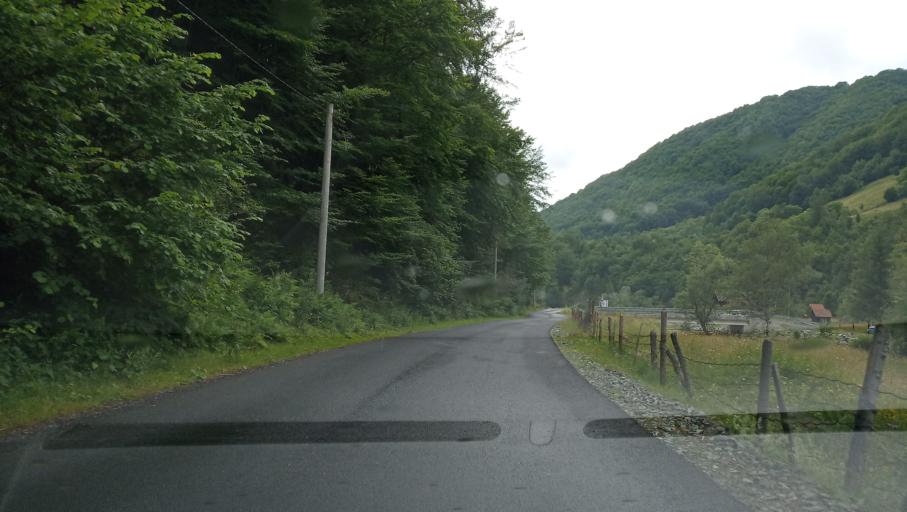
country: RO
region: Hunedoara
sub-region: Oras Petrila
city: Petrila
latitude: 45.4165
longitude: 23.4603
